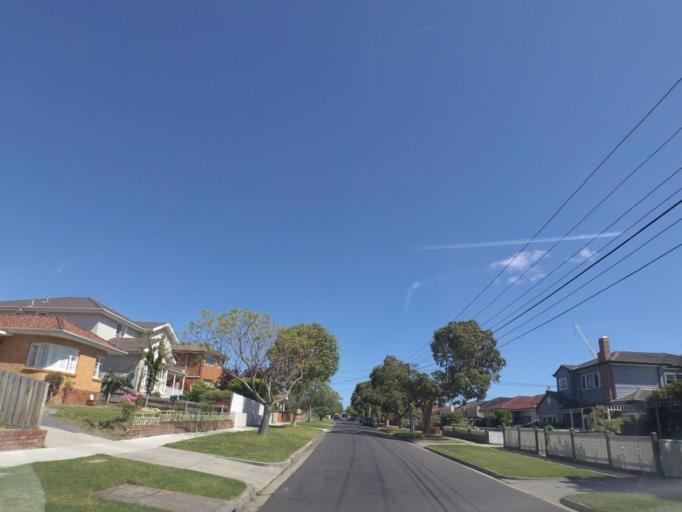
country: AU
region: Victoria
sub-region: Monash
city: Chadstone
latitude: -37.8967
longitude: 145.0970
